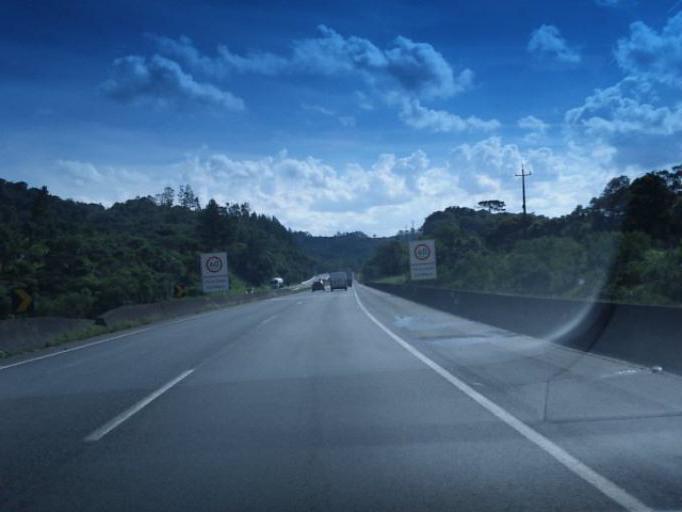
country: BR
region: Parana
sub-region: Campina Grande Do Sul
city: Campina Grande do Sul
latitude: -25.1647
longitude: -48.8626
